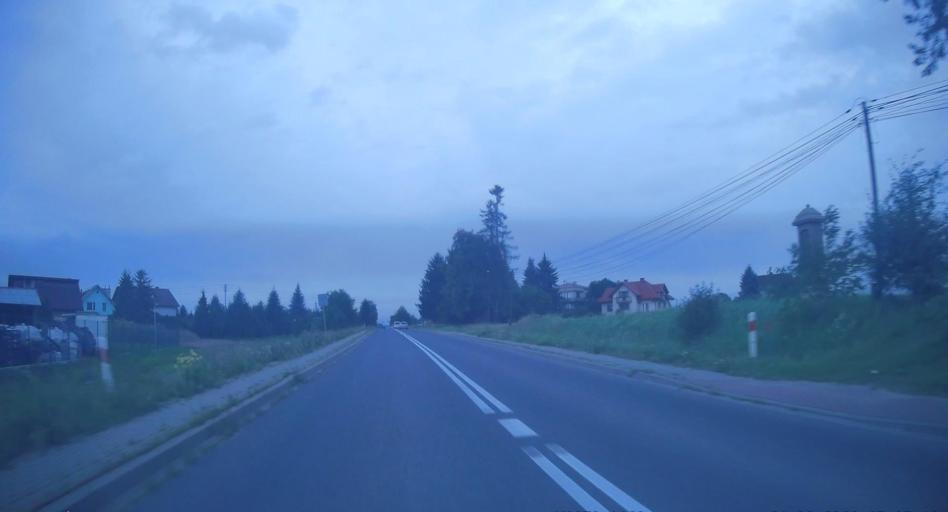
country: PL
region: Lesser Poland Voivodeship
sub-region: Powiat wielicki
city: Targowisko
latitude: 49.9776
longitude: 20.2962
